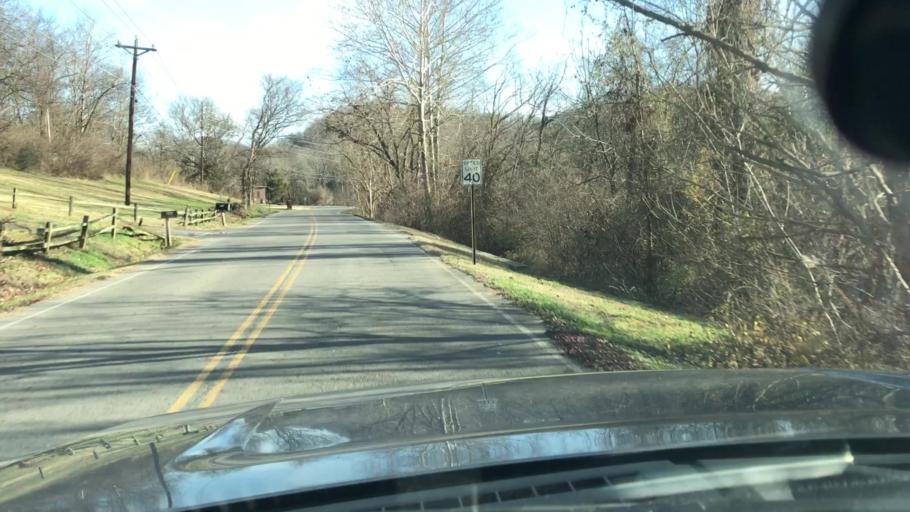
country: US
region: Tennessee
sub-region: Davidson County
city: Forest Hills
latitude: 36.0038
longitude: -86.8407
